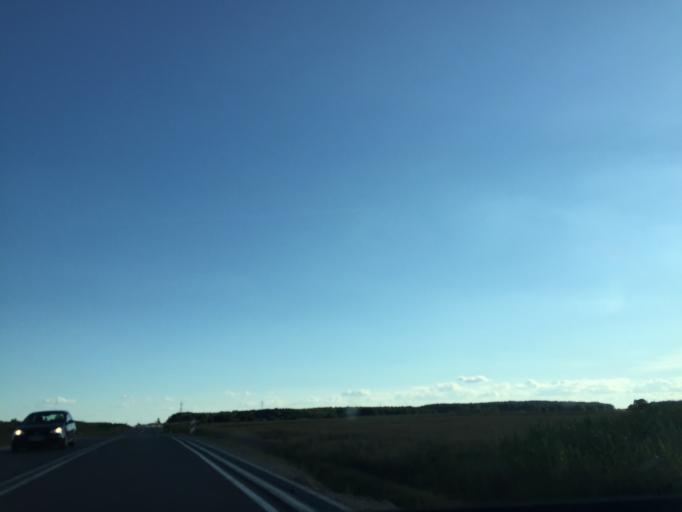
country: PL
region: Podlasie
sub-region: Powiat grajewski
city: Szczuczyn
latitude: 53.4968
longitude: 22.2282
